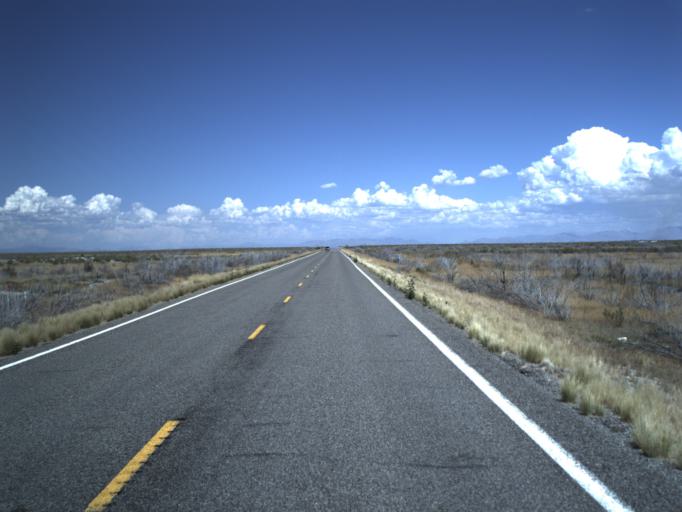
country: US
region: Utah
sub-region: Millard County
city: Delta
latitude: 39.2827
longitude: -112.8418
